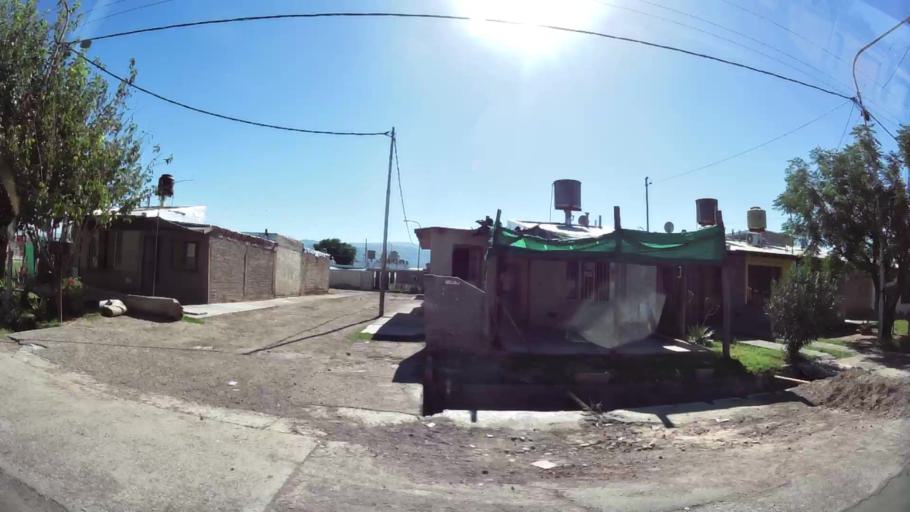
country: AR
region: Mendoza
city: Las Heras
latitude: -32.8392
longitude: -68.8110
